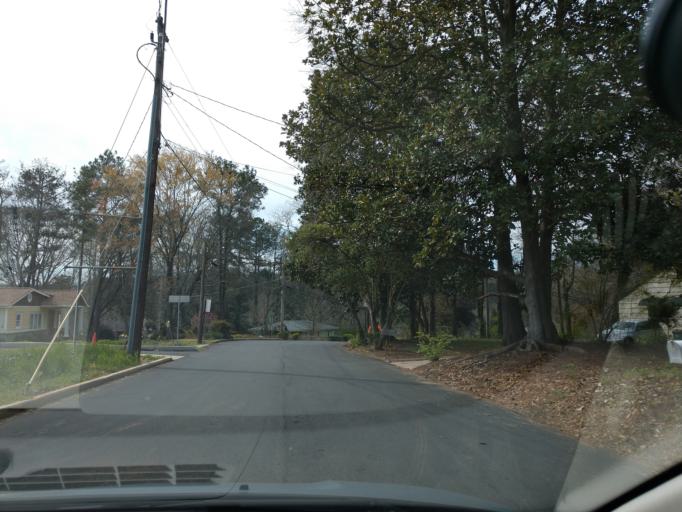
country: US
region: Georgia
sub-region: Fulton County
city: Atlanta
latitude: 33.7222
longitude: -84.3635
